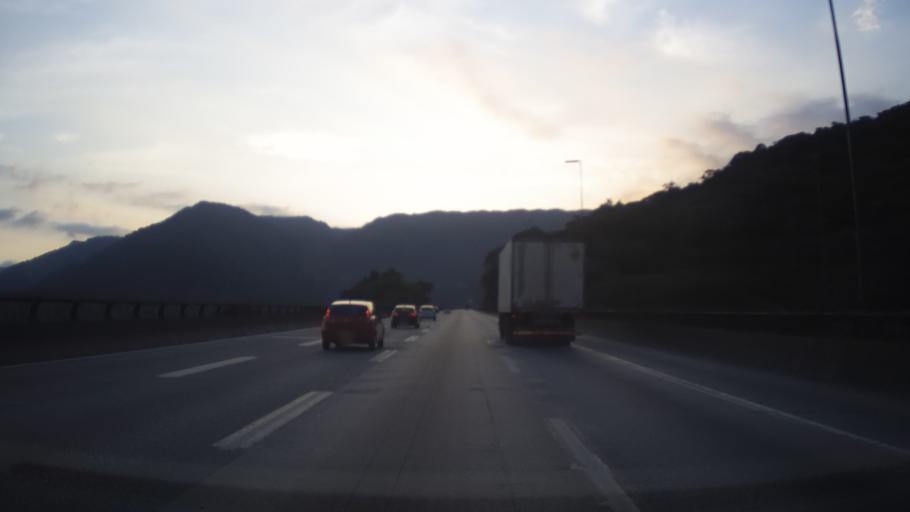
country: BR
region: Sao Paulo
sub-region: Cubatao
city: Cubatao
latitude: -23.8994
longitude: -46.4829
